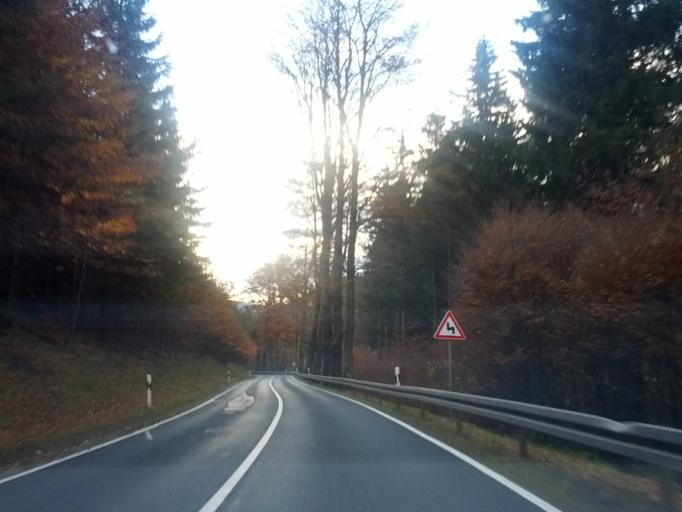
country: DE
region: Thuringia
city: Brotterode
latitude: 50.8401
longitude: 10.4736
